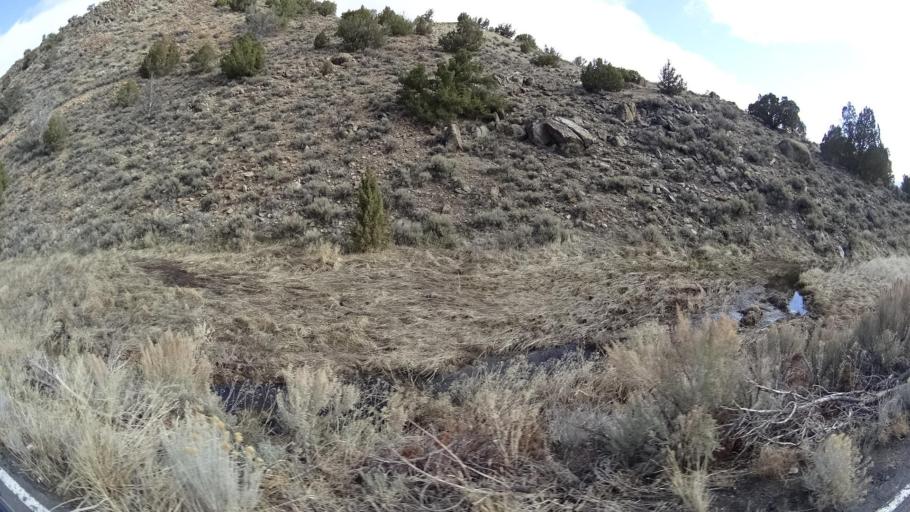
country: US
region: Nevada
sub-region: Washoe County
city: Cold Springs
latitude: 39.9022
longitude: -119.9881
